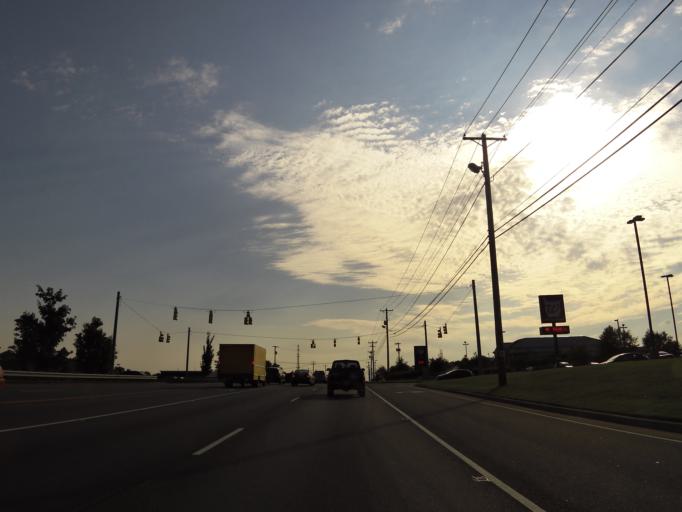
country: US
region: Tennessee
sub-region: Blount County
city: Maryville
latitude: 35.7175
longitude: -84.0139
